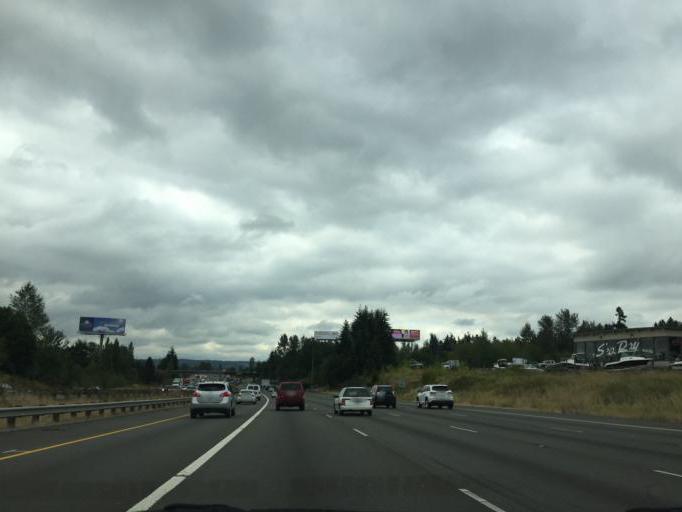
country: US
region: Washington
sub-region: Pierce County
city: Fife Heights
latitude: 47.2553
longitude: -122.3314
